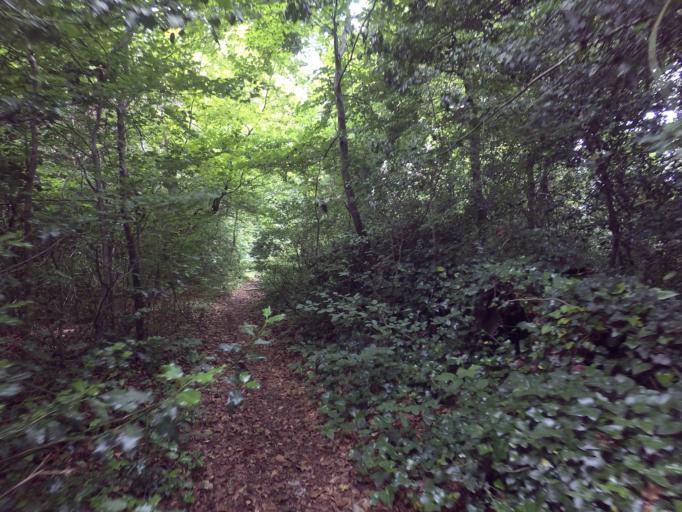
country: IE
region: Leinster
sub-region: Fingal County
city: Blanchardstown
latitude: 53.3864
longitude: -6.3675
